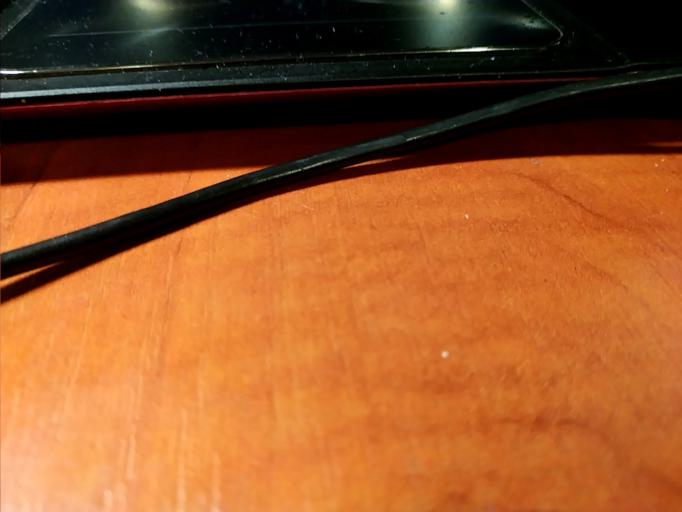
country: RU
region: Tverskaya
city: Tver
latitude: 56.8180
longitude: 35.9848
